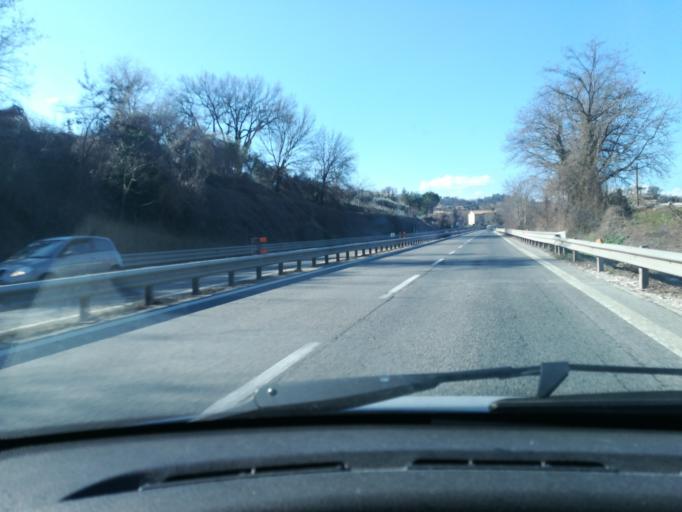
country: IT
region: The Marches
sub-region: Provincia di Macerata
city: Tolentino
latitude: 43.2061
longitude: 13.2991
